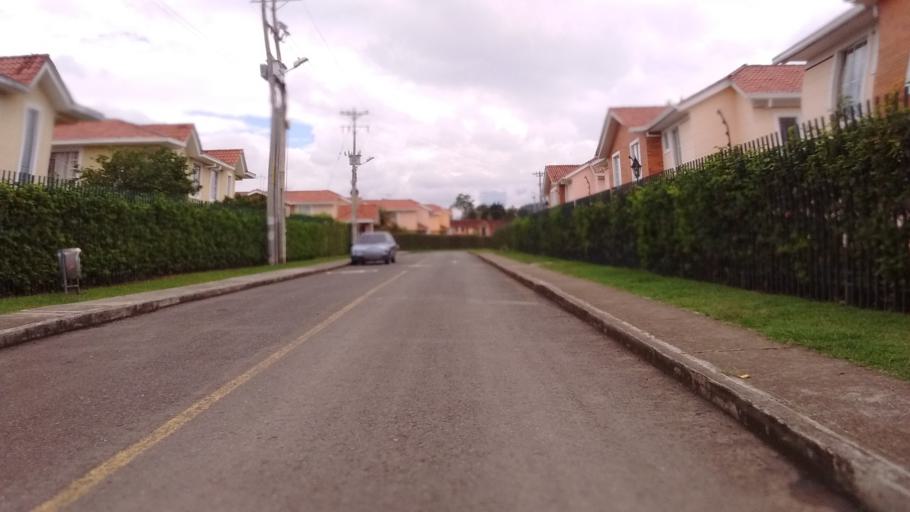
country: CO
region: Cauca
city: Popayan
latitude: 2.4784
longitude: -76.5815
